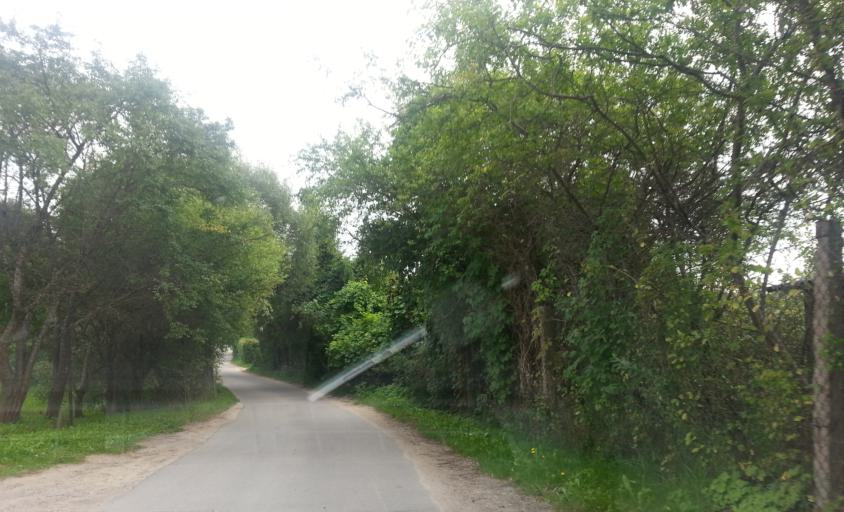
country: LT
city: Grigiskes
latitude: 54.7574
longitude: 25.0236
